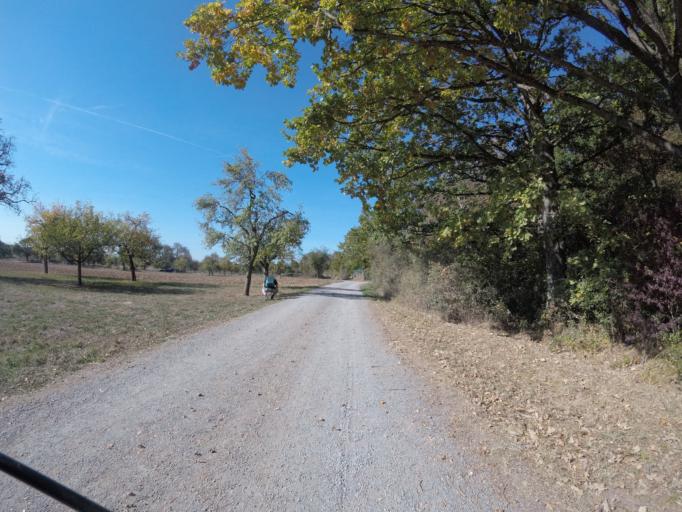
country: DE
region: Baden-Wuerttemberg
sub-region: Karlsruhe Region
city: Sternenfels
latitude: 49.0143
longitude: 8.8519
